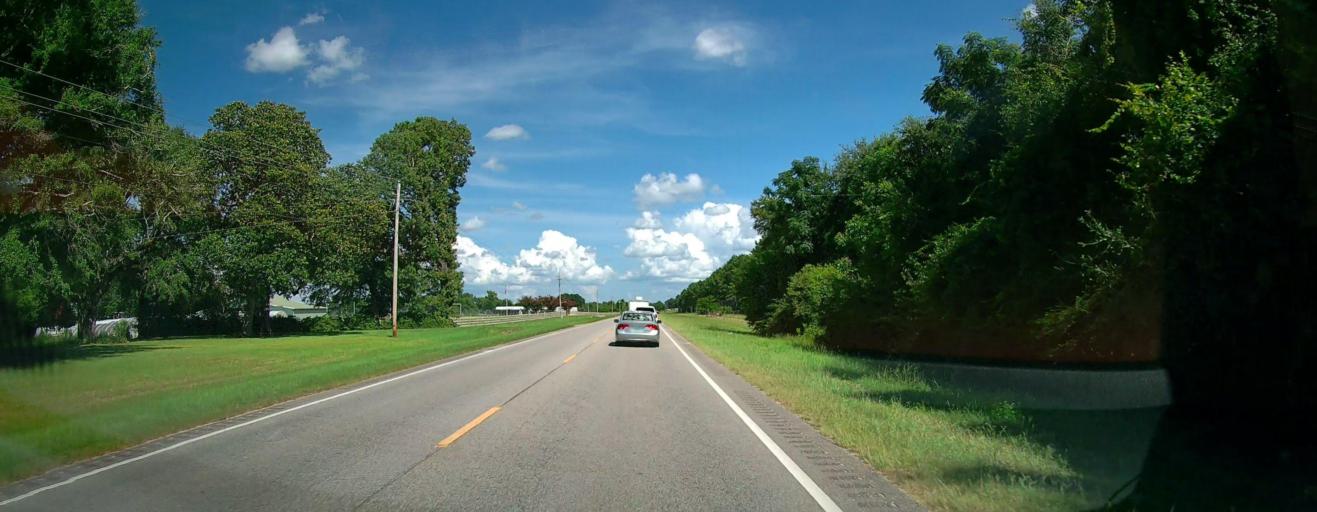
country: US
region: Alabama
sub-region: Elmore County
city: Tallassee
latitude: 32.3926
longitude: -85.9004
